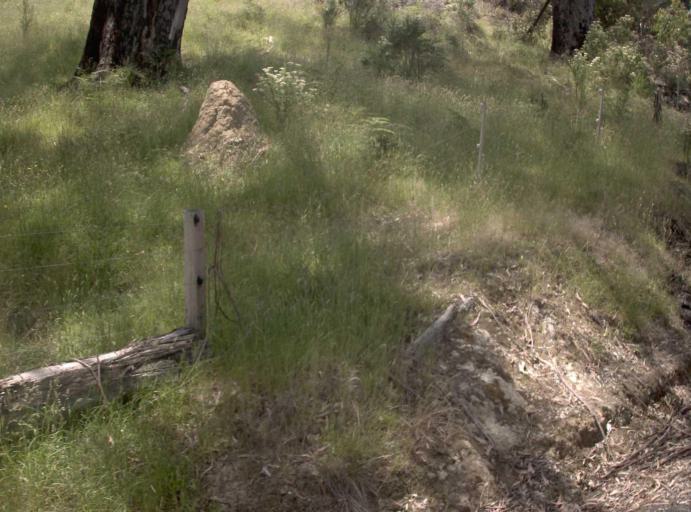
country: AU
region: New South Wales
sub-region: Bombala
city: Bombala
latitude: -37.3607
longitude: 149.0214
